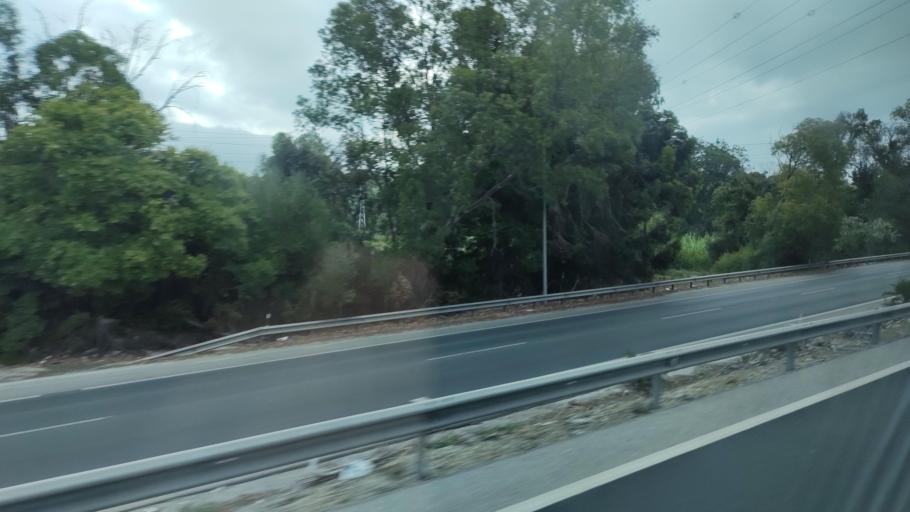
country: ES
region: Andalusia
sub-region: Provincia de Cadiz
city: San Roque
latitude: 36.1865
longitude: -5.3841
